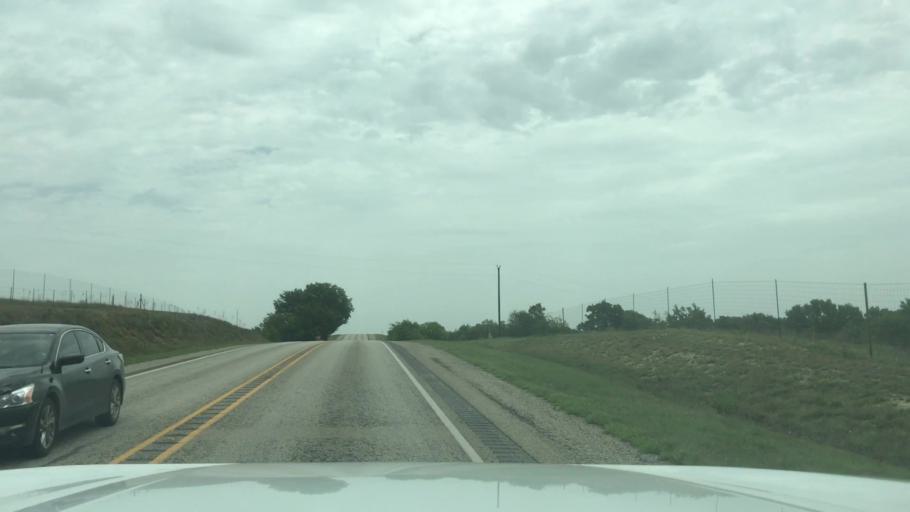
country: US
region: Texas
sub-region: Hamilton County
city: Hico
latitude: 32.0547
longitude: -98.1775
